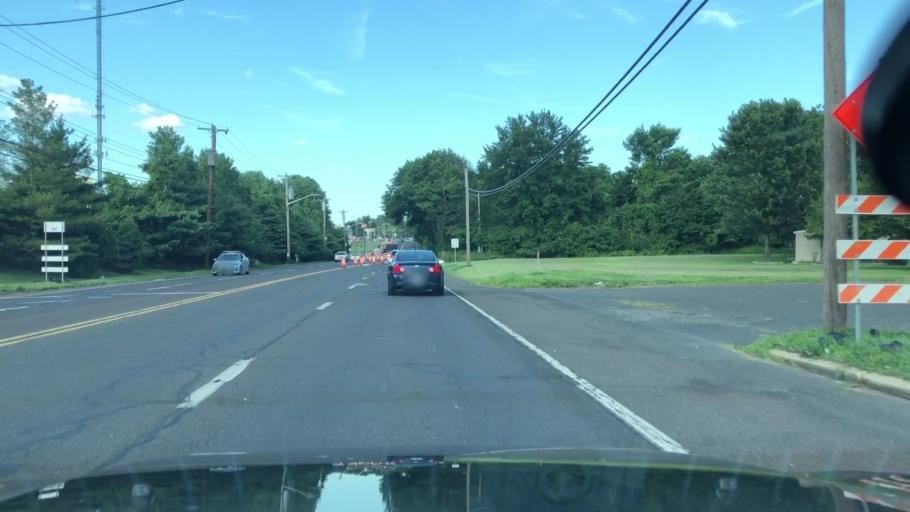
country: US
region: Pennsylvania
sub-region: Bucks County
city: Fairless Hills
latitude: 40.1866
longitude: -74.8495
